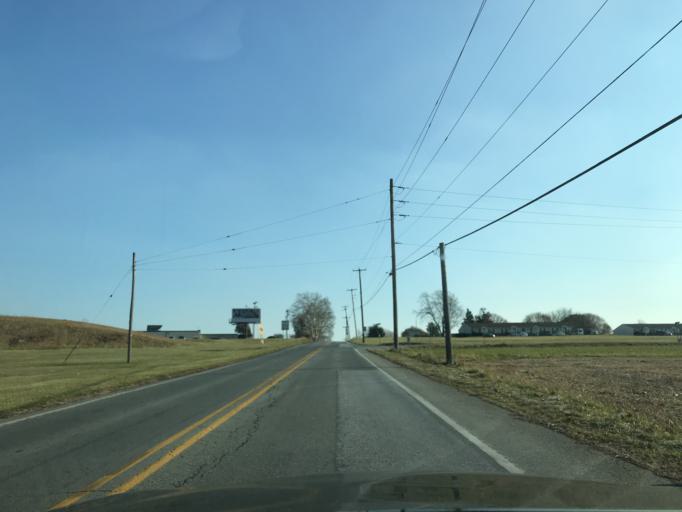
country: US
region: Pennsylvania
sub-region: York County
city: Loganville
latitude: 39.8230
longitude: -76.6967
